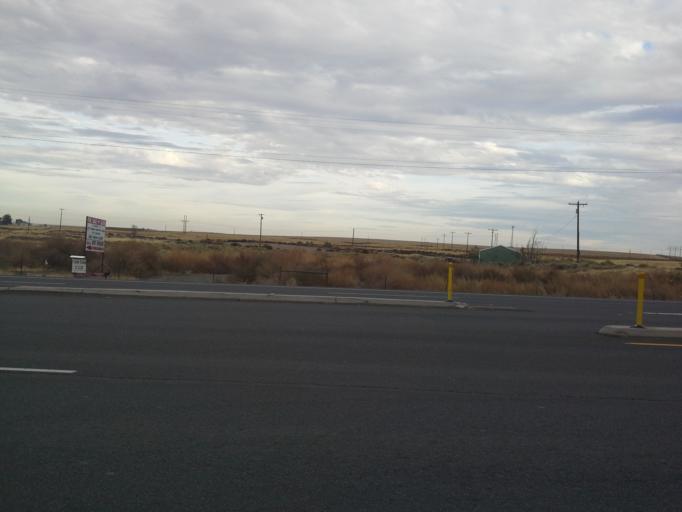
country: US
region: Oregon
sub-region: Umatilla County
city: Stanfield
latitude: 45.7658
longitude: -119.2048
